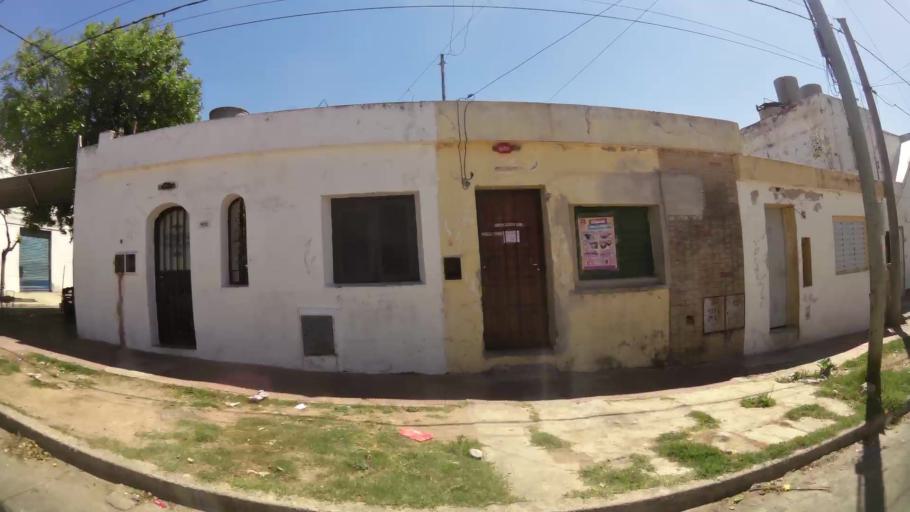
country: AR
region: Cordoba
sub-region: Departamento de Capital
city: Cordoba
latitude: -31.4319
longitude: -64.2086
